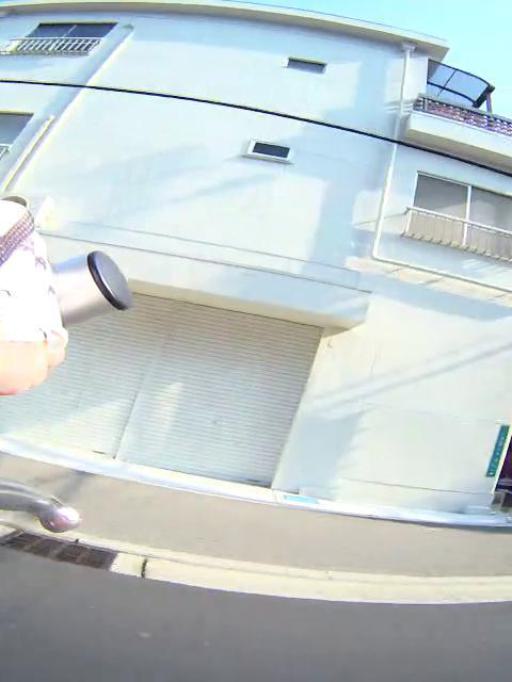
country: JP
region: Osaka
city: Suita
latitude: 34.7349
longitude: 135.4840
